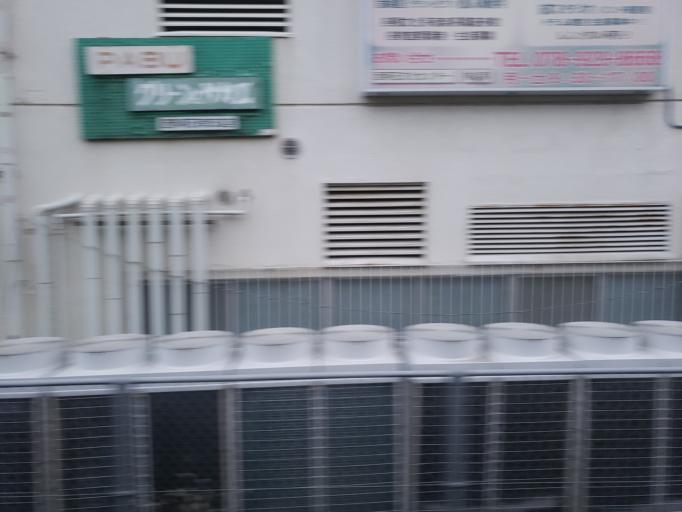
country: JP
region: Hyogo
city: Akashi
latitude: 34.6652
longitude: 134.9608
